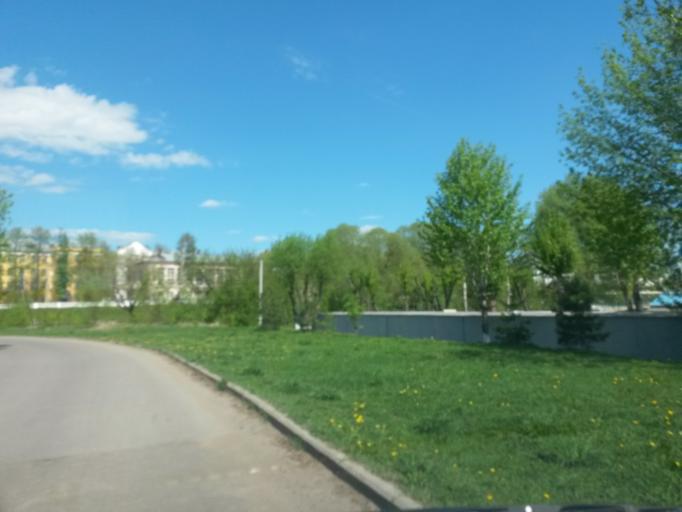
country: RU
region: Jaroslavl
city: Yaroslavl
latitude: 57.6180
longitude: 39.8729
